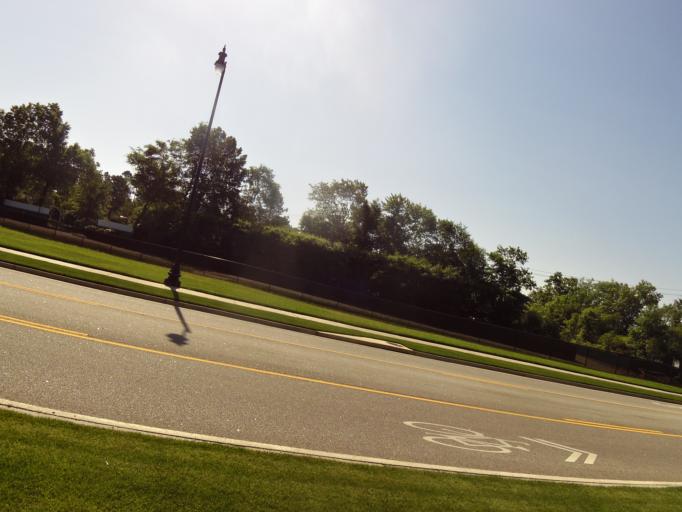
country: US
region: Georgia
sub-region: Columbia County
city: Martinez
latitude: 33.4994
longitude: -82.0313
